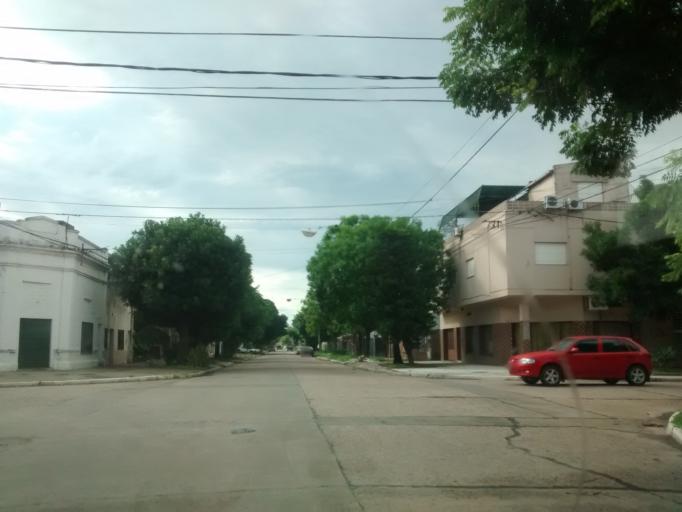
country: AR
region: Chaco
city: Resistencia
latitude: -27.4417
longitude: -58.9953
